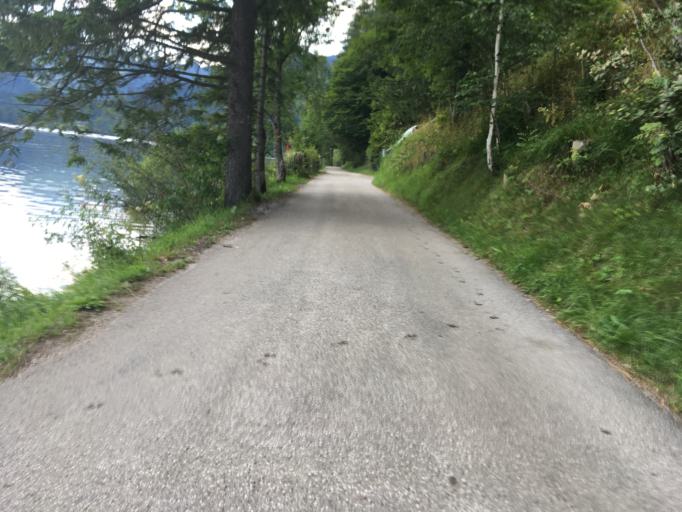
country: AT
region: Lower Austria
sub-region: Politischer Bezirk Lilienfeld
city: Mitterbach am Erlaufsee
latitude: 47.7934
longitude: 15.2757
